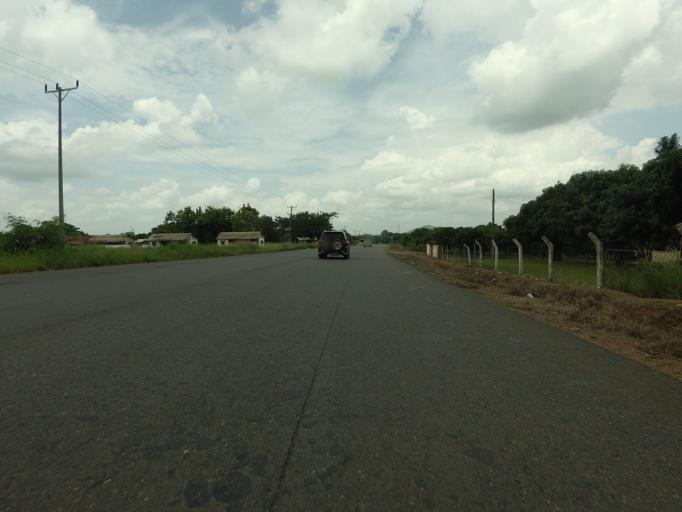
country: GH
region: Volta
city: Ho
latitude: 6.4204
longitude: 0.1720
